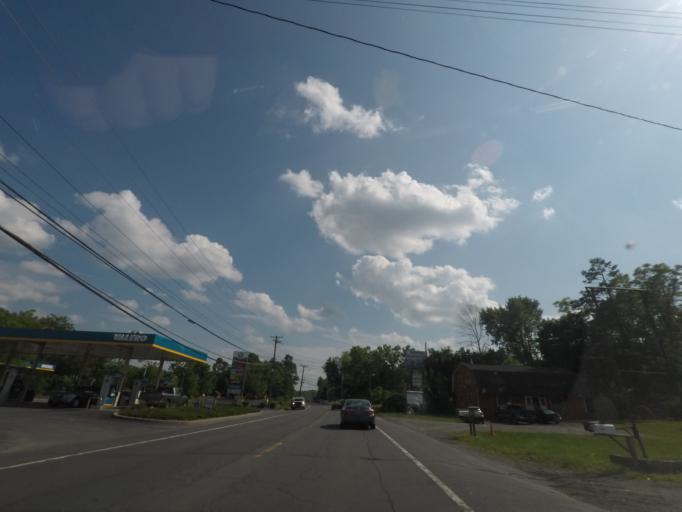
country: US
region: New York
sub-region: Orange County
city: Balmville
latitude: 41.5557
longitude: -74.0047
